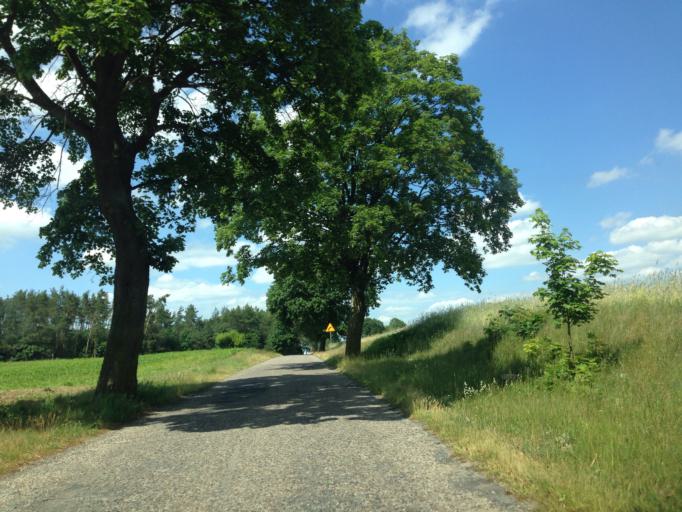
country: PL
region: Kujawsko-Pomorskie
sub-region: Powiat brodnicki
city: Bartniczka
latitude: 53.2764
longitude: 19.6900
